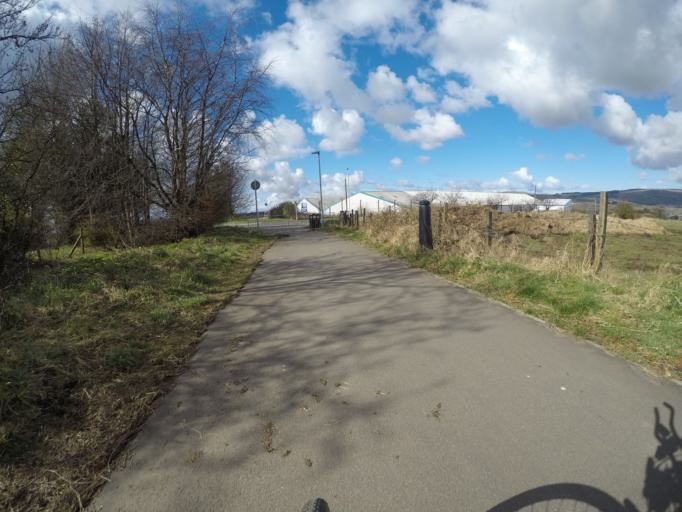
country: GB
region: Scotland
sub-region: North Ayrshire
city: Beith
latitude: 55.7441
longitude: -4.6458
